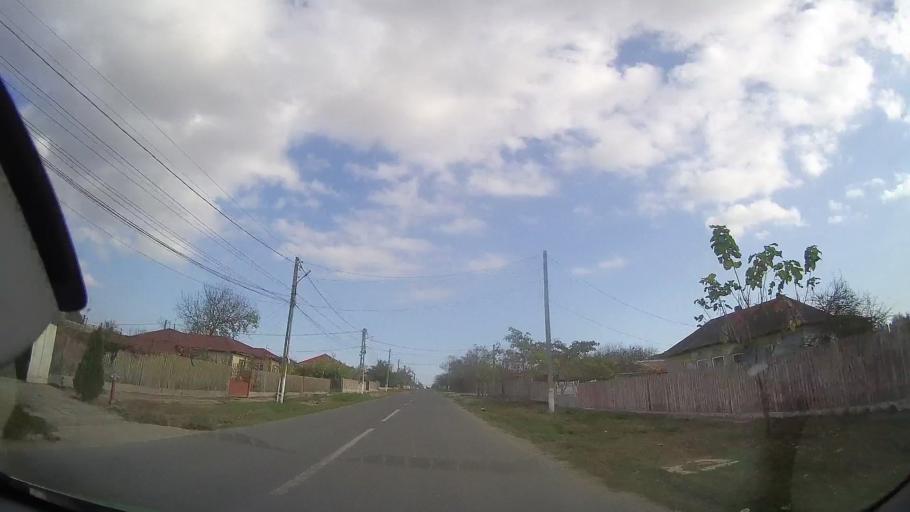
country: RO
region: Constanta
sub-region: Comuna Pecineaga
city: Pecineaga
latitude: 43.8952
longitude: 28.5000
